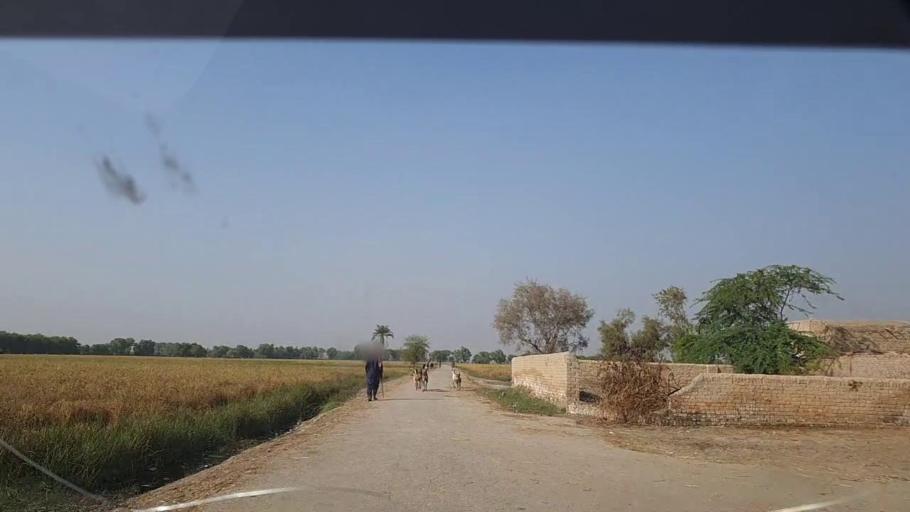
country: PK
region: Sindh
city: Shikarpur
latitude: 28.1187
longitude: 68.5834
